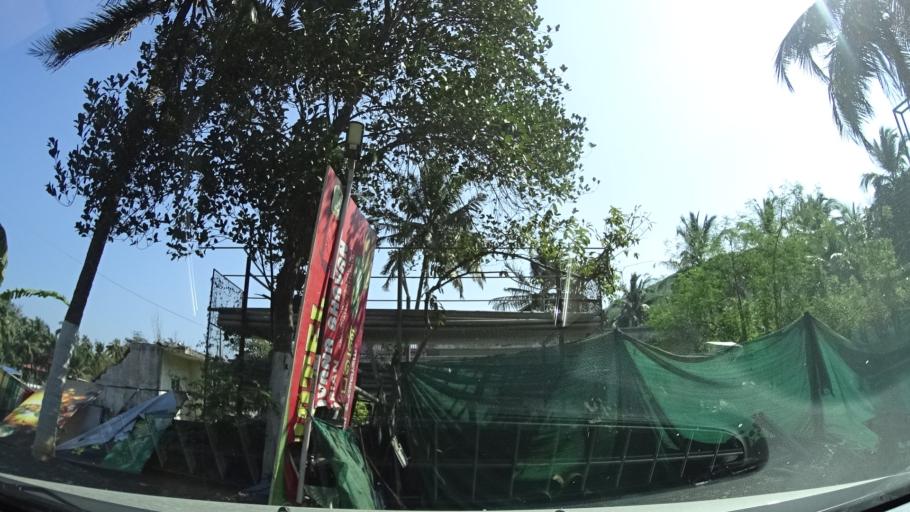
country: IN
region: Kerala
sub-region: Thrissur District
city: Trichur
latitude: 10.5469
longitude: 76.2960
